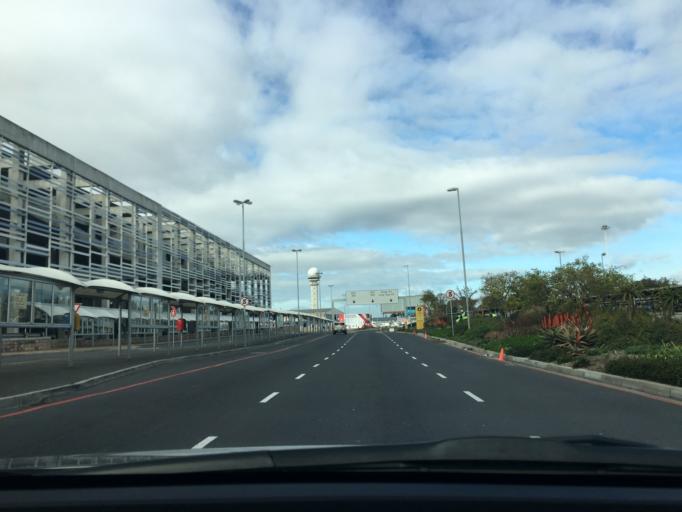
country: ZA
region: Western Cape
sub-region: City of Cape Town
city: Lansdowne
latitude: -33.9706
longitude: 18.5957
